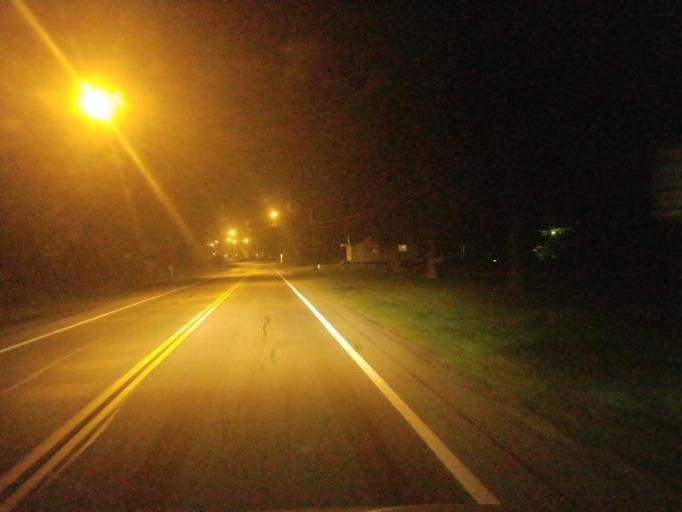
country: US
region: Ohio
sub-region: Carroll County
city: Malvern
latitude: 40.7632
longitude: -81.1877
